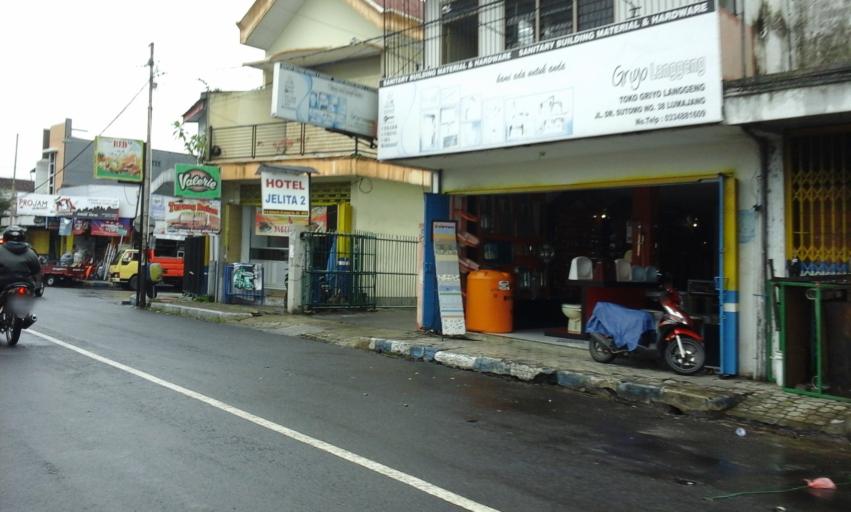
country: ID
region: East Java
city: Lumajang
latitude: -8.1294
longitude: 113.2229
